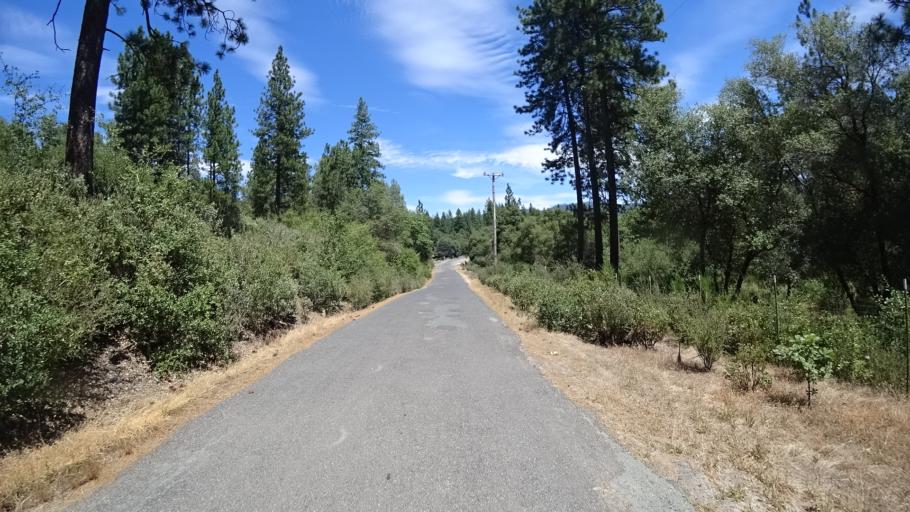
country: US
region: California
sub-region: Calaveras County
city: Forest Meadows
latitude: 38.2119
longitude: -120.4513
